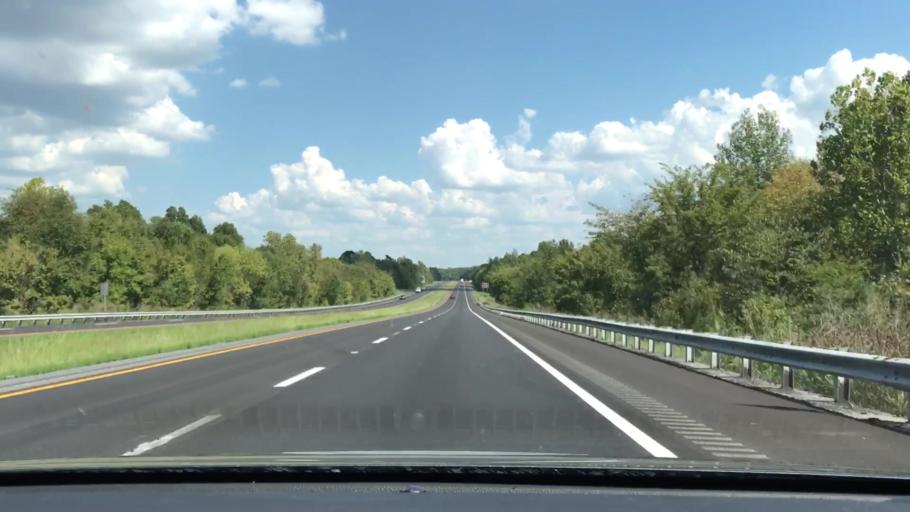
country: US
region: Kentucky
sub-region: Lyon County
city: Eddyville
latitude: 37.0873
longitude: -88.0613
